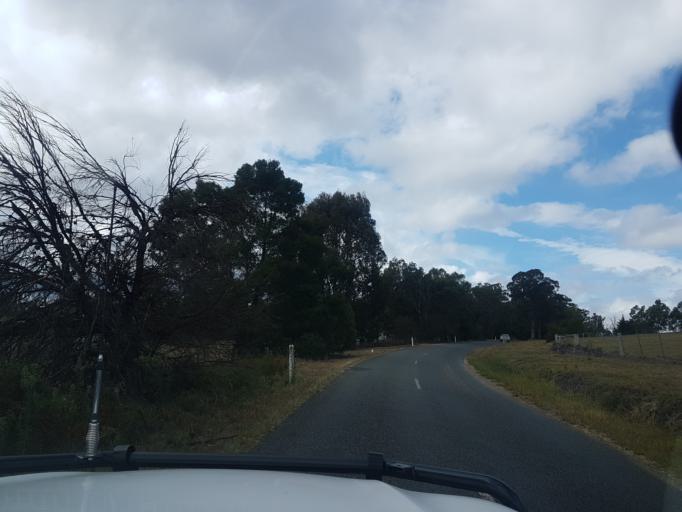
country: AU
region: Victoria
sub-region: East Gippsland
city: Bairnsdale
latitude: -37.7873
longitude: 147.5725
